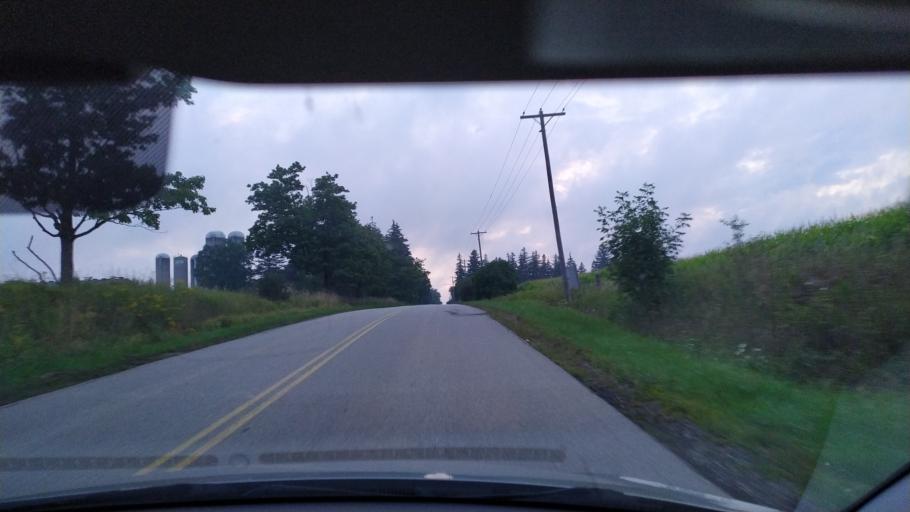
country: CA
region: Ontario
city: Kitchener
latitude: 43.3529
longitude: -80.6810
